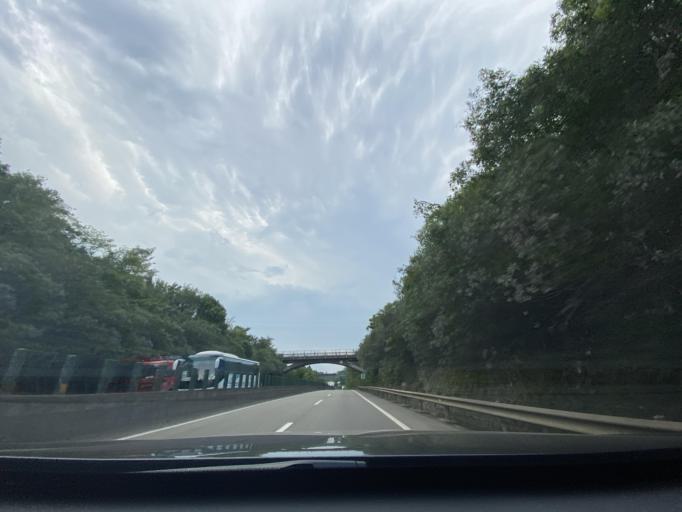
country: CN
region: Sichuan
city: Neijiang
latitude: 29.6633
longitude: 104.9797
